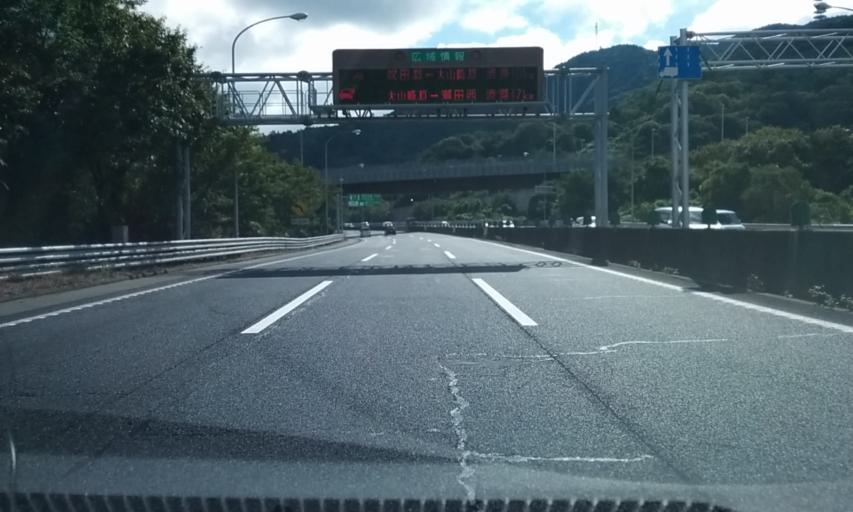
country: JP
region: Hyogo
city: Sandacho
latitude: 34.8359
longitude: 135.2599
